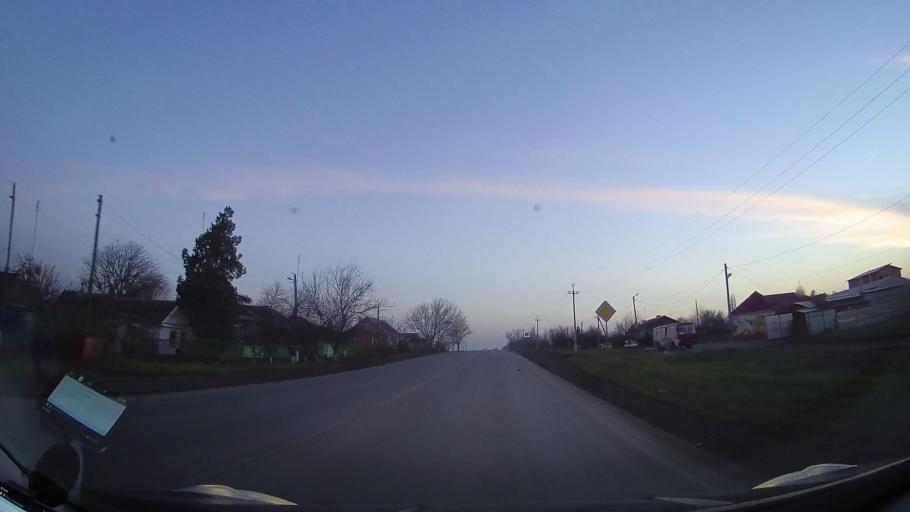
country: RU
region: Rostov
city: Zernograd
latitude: 46.8368
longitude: 40.2994
